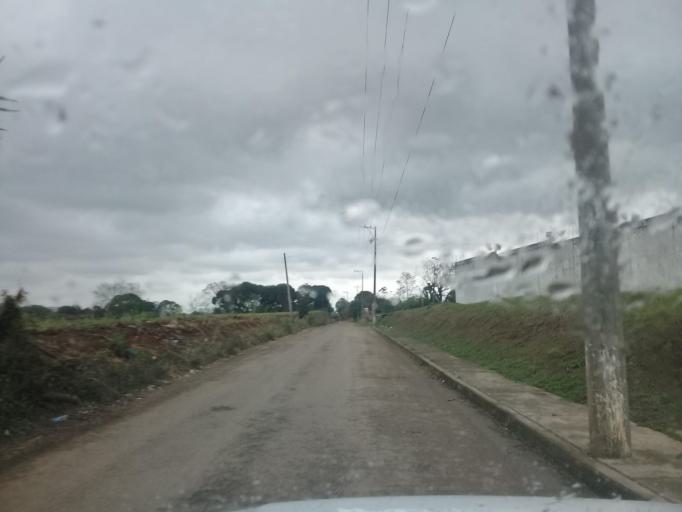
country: MX
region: Veracruz
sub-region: Amatlan de los Reyes
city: Centro de Readaptacion Social
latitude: 18.8399
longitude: -96.9402
